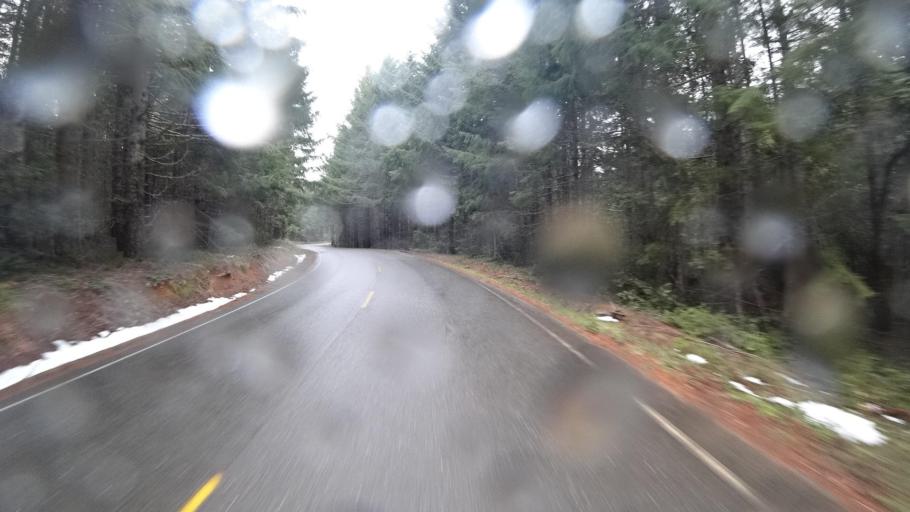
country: US
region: California
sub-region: Humboldt County
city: Willow Creek
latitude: 41.1792
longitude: -123.8161
